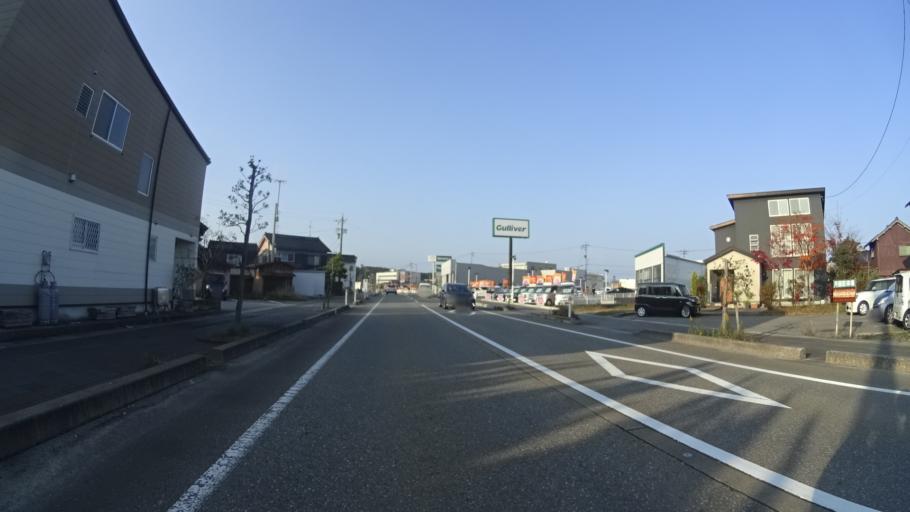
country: JP
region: Ishikawa
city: Nanao
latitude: 37.0514
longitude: 136.9562
